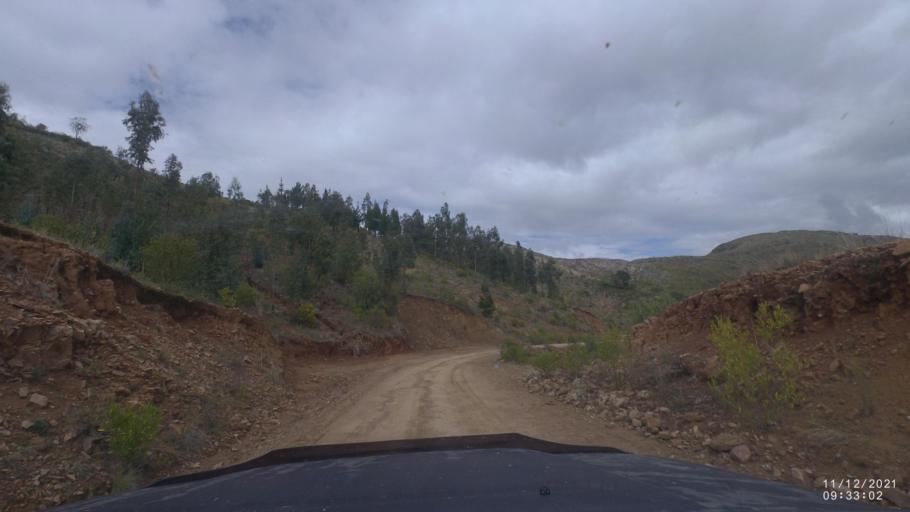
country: BO
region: Cochabamba
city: Tarata
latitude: -17.8405
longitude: -65.9901
